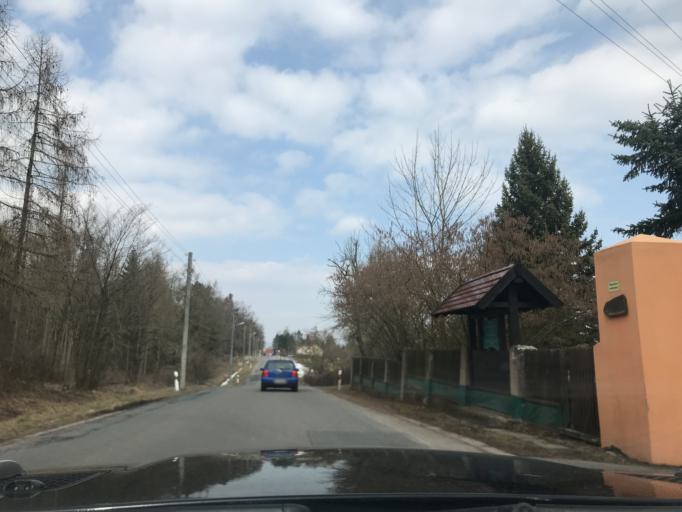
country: DE
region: Thuringia
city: Oberdorla
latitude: 51.1973
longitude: 10.3963
